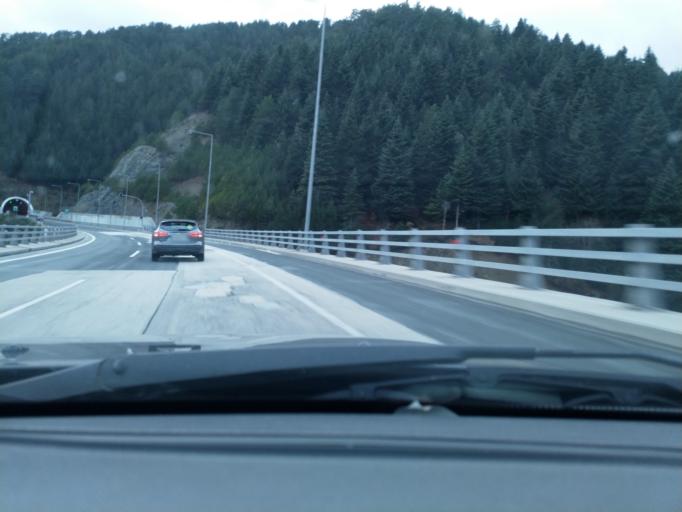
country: GR
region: Epirus
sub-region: Nomos Ioanninon
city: Metsovo
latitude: 39.7896
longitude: 21.2629
